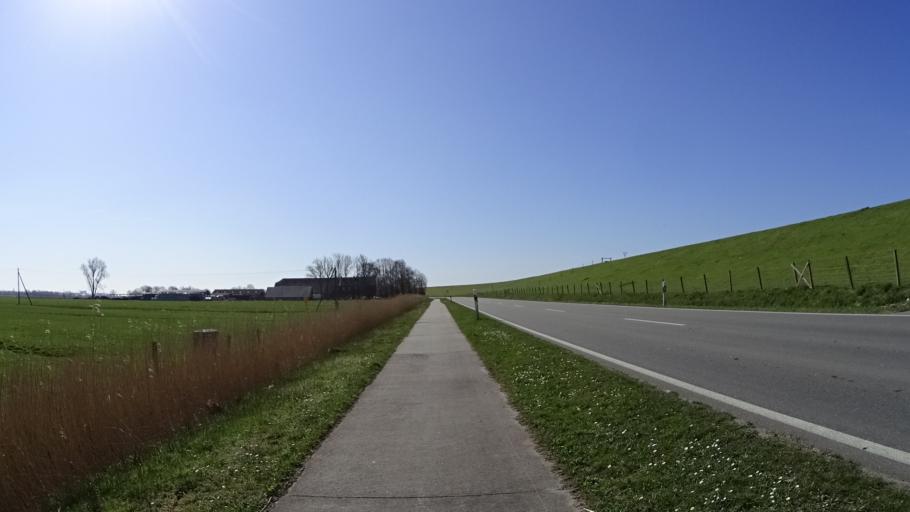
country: DE
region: Lower Saxony
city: Jemgum
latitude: 53.2514
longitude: 7.4054
